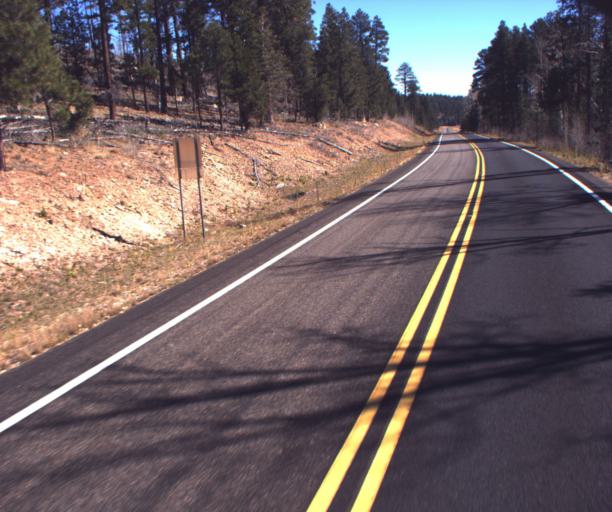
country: US
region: Arizona
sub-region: Coconino County
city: Grand Canyon
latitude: 36.5437
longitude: -112.1749
